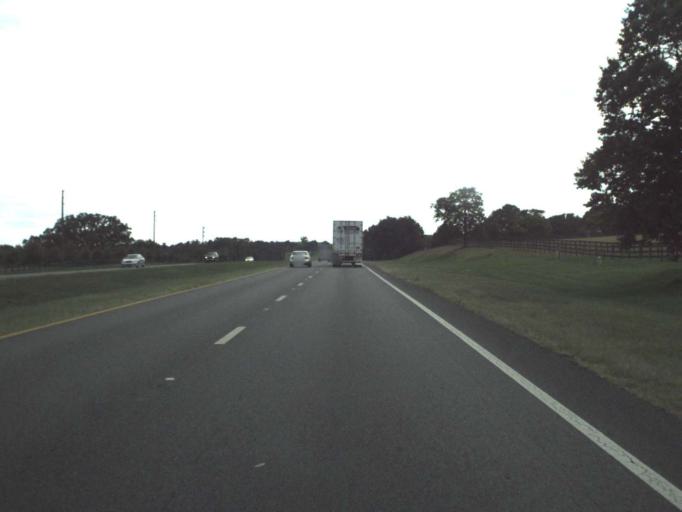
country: US
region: Florida
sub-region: Marion County
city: Citra
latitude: 29.3201
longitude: -82.1519
